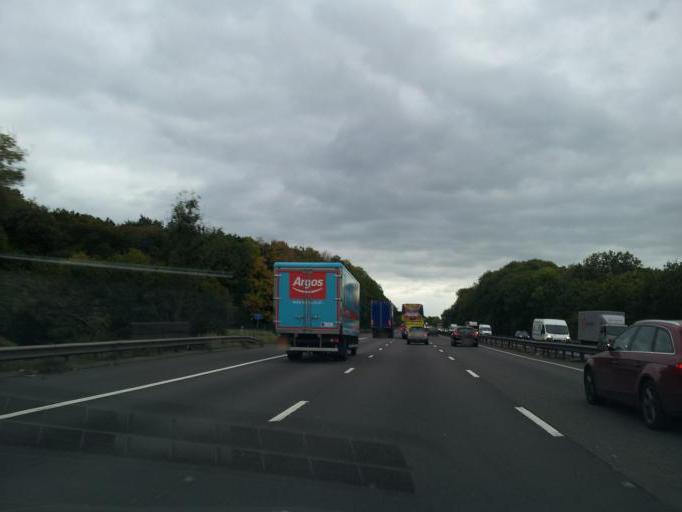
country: GB
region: England
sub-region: Northamptonshire
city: Hartwell
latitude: 52.1462
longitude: -0.8395
